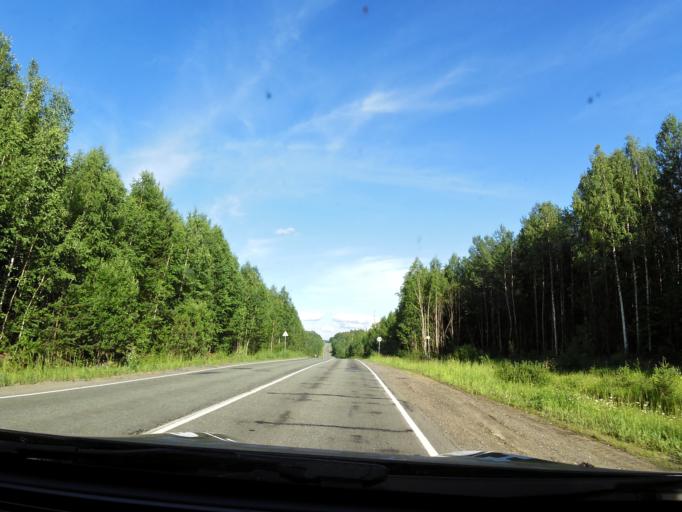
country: RU
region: Kirov
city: Chernaya Kholunitsa
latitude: 58.8655
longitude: 51.5760
